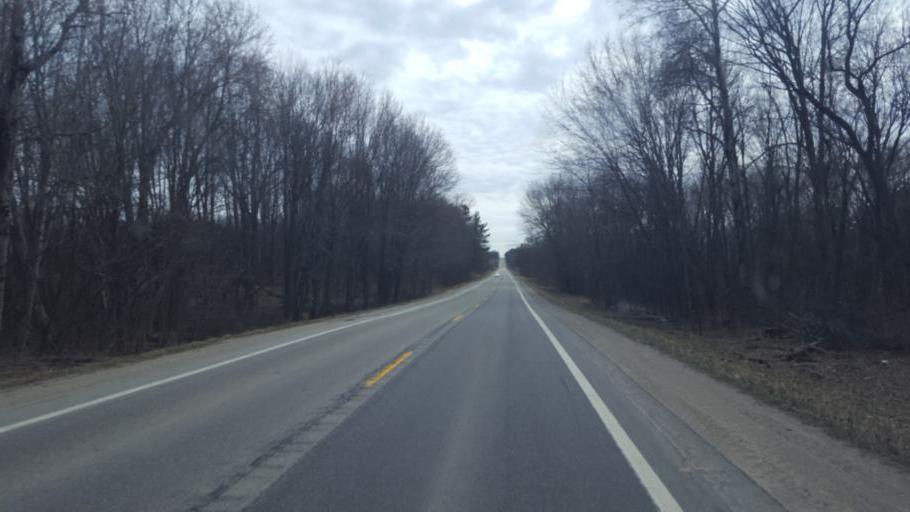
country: US
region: Michigan
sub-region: Isabella County
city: Lake Isabella
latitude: 43.6964
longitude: -85.1467
